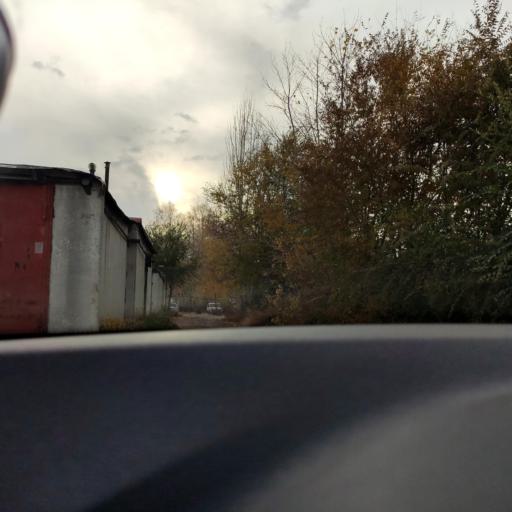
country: RU
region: Samara
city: Smyshlyayevka
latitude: 53.1892
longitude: 50.2775
